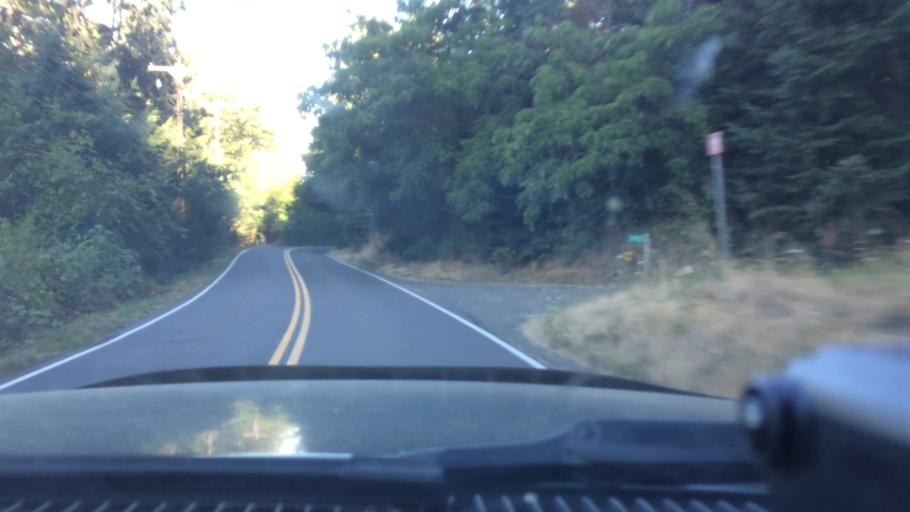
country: US
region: Oregon
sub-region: Yamhill County
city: Newberg
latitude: 45.3311
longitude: -122.9352
